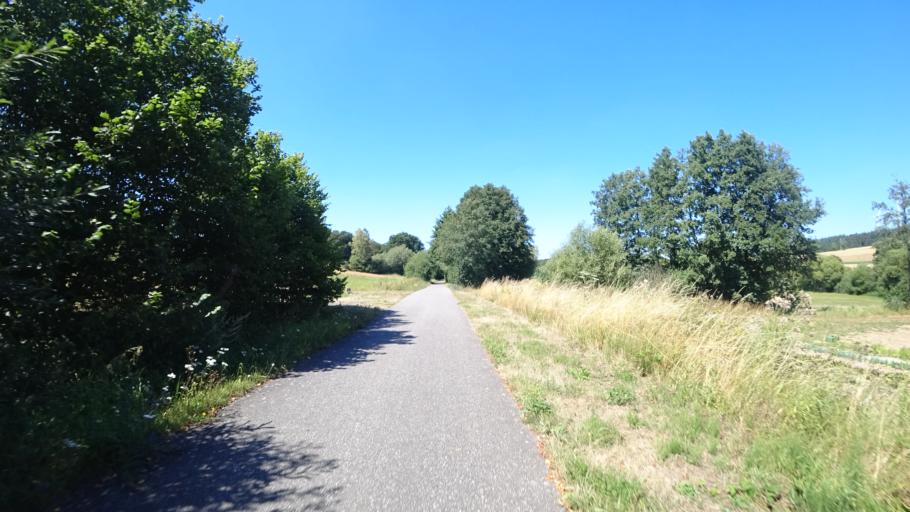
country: DE
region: Rheinland-Pfalz
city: Neuerkirch
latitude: 50.0163
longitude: 7.4861
